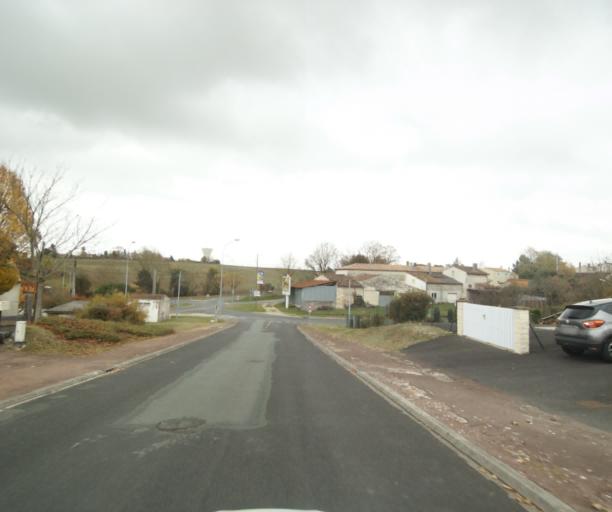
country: FR
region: Poitou-Charentes
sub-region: Departement de la Charente-Maritime
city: Saintes
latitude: 45.7377
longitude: -0.6580
